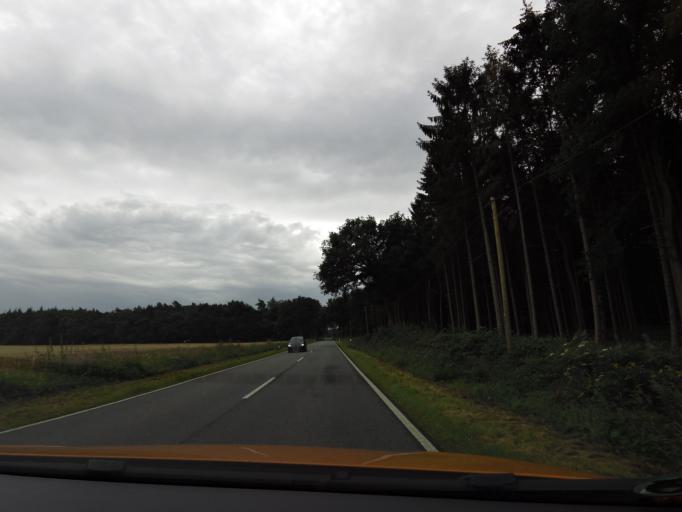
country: DE
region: Lower Saxony
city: Dunsen
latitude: 52.8852
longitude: 8.6273
